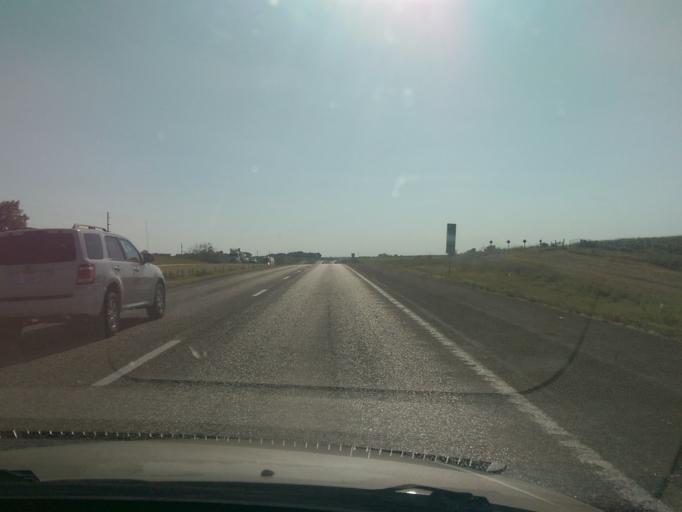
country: US
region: Missouri
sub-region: Lafayette County
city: Concordia
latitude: 38.9934
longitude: -93.6010
